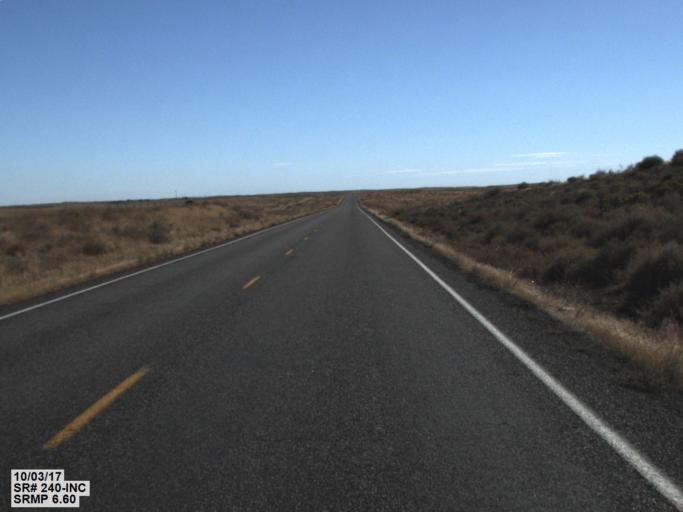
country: US
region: Washington
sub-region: Benton County
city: Benton City
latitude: 46.5081
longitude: -119.6434
